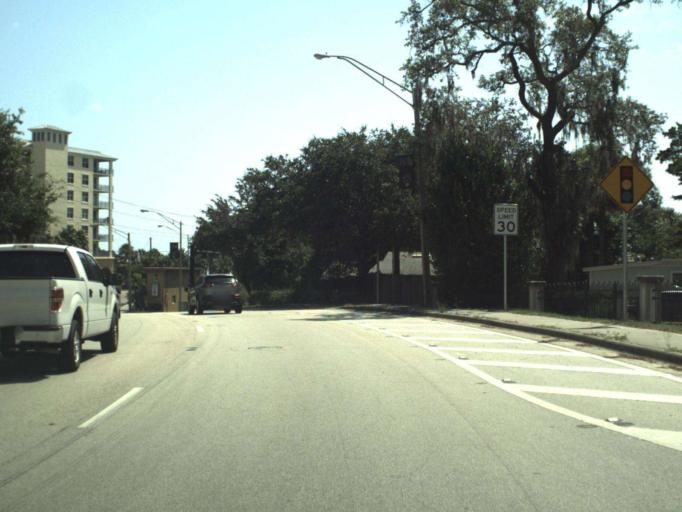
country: US
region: Florida
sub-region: Brevard County
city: Indian Harbour Beach
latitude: 28.1293
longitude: -80.6263
